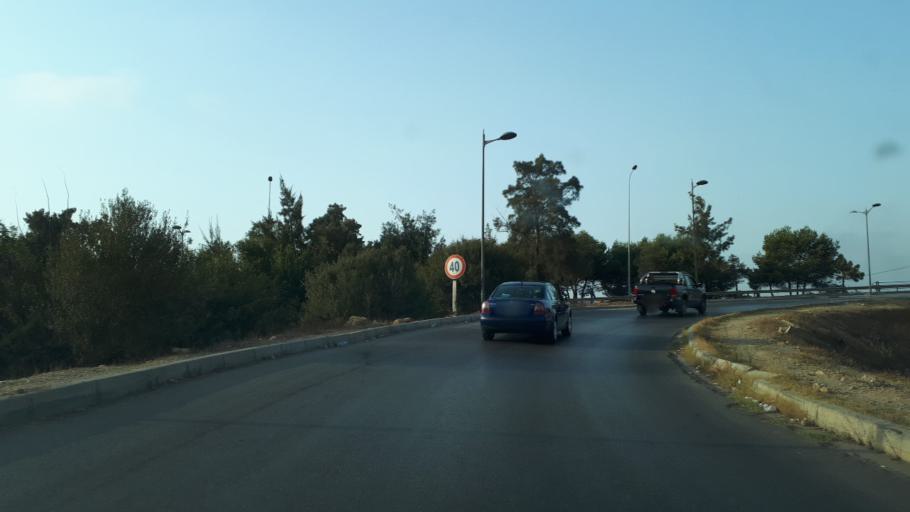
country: DZ
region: Alger
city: Dar el Beida
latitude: 36.7267
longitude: 3.2103
